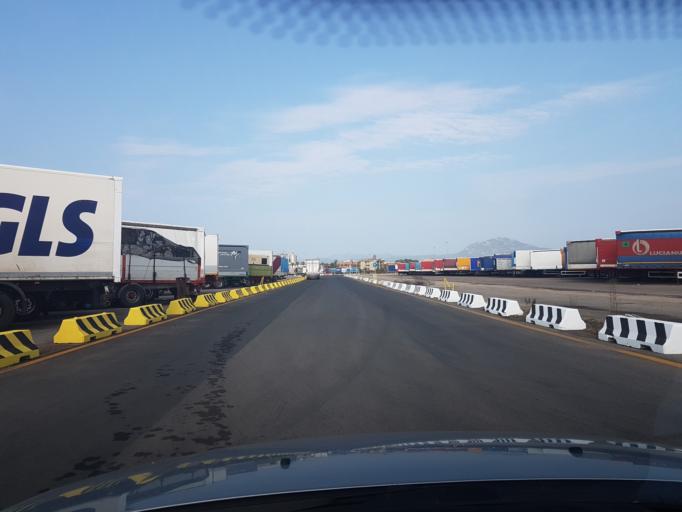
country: IT
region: Sardinia
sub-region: Provincia di Olbia-Tempio
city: Olbia
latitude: 40.9243
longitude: 9.5181
